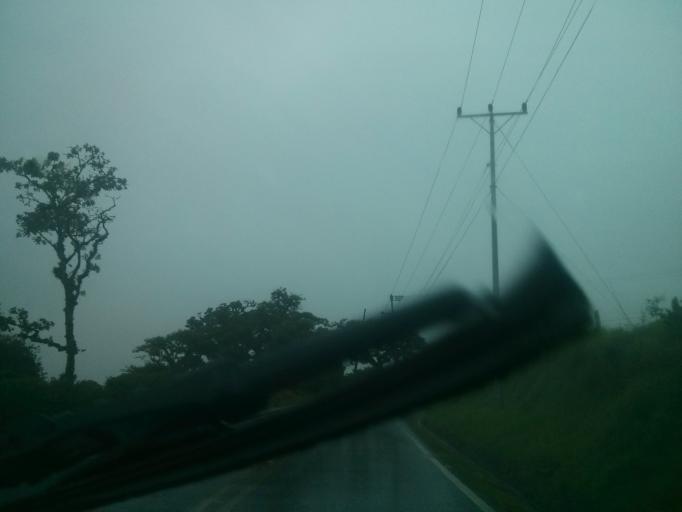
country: CR
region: Heredia
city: Santo Domingo
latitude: 10.1834
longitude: -84.1548
